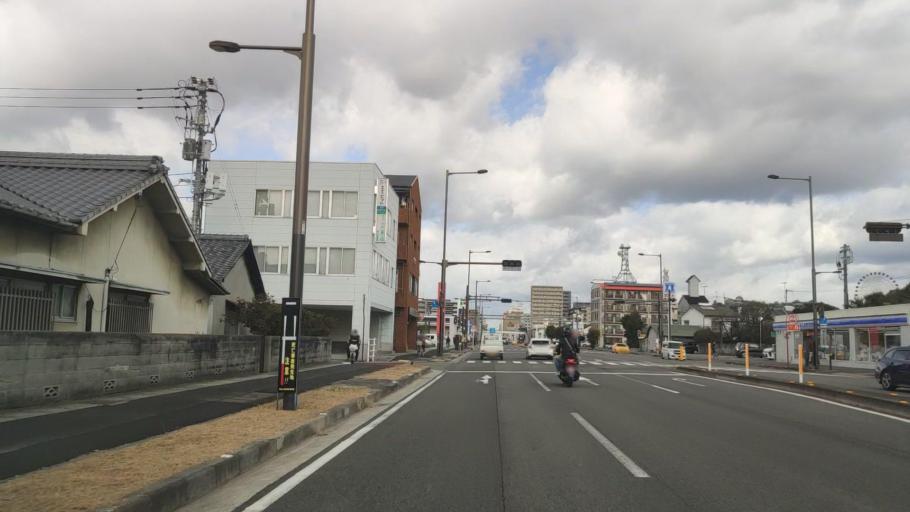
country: JP
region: Ehime
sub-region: Shikoku-chuo Shi
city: Matsuyama
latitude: 33.8288
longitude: 132.7588
